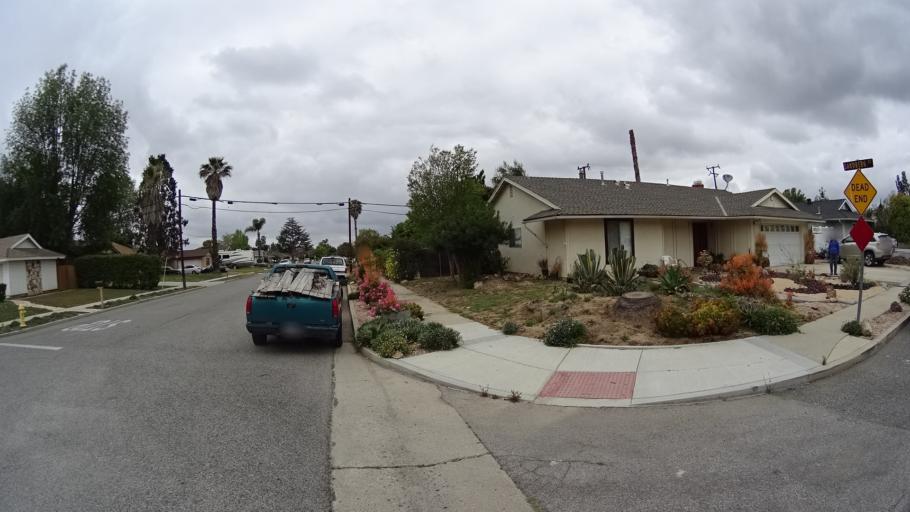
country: US
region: California
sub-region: Ventura County
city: Thousand Oaks
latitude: 34.2136
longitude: -118.8777
